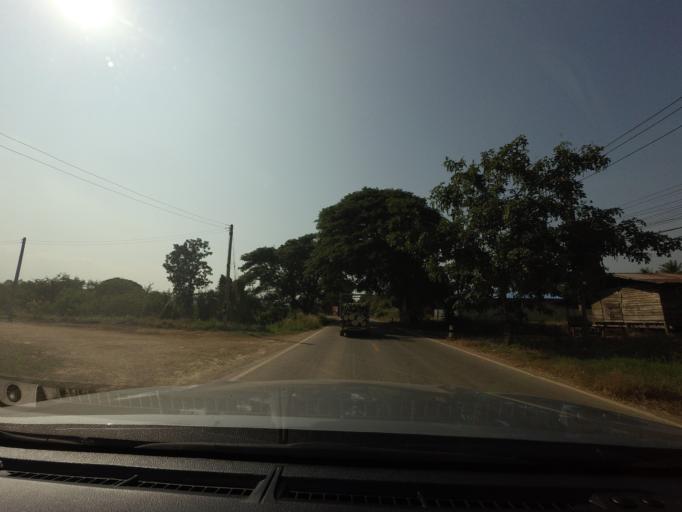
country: TH
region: Sukhothai
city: Kong Krailat
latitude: 16.8545
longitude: 99.9424
